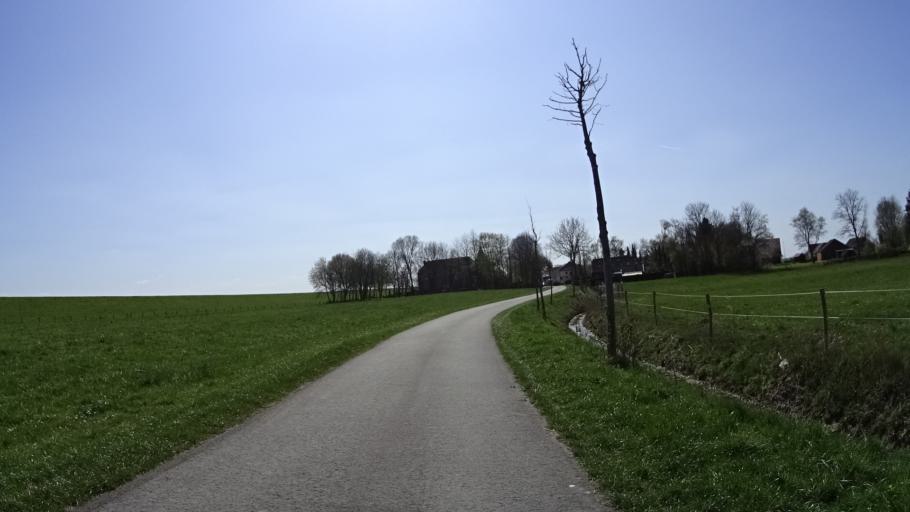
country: DE
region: Lower Saxony
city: Leer
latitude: 53.2018
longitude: 7.4038
